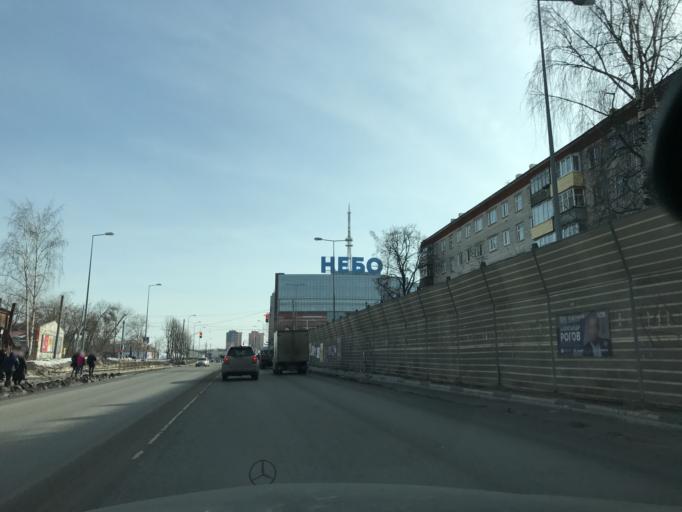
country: RU
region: Nizjnij Novgorod
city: Nizhniy Novgorod
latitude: 56.3105
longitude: 43.9824
